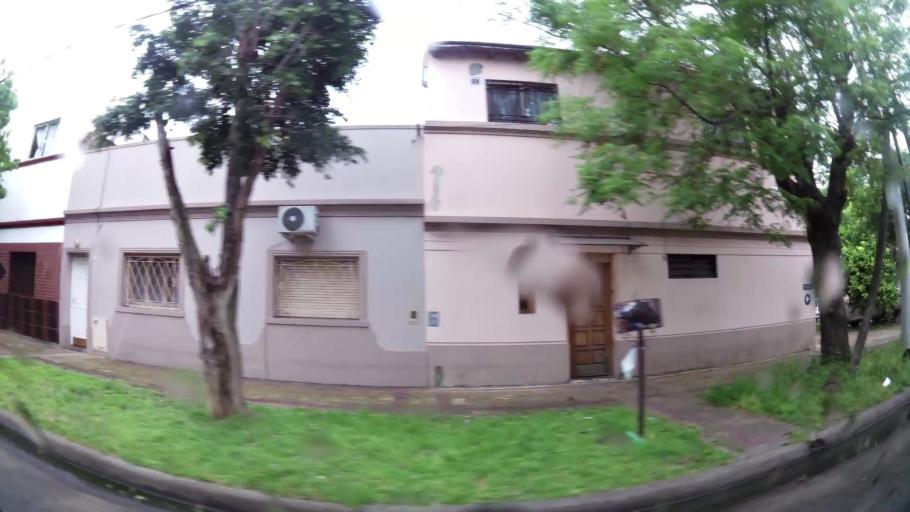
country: AR
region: Buenos Aires
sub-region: Partido de Lanus
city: Lanus
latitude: -34.7005
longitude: -58.4006
